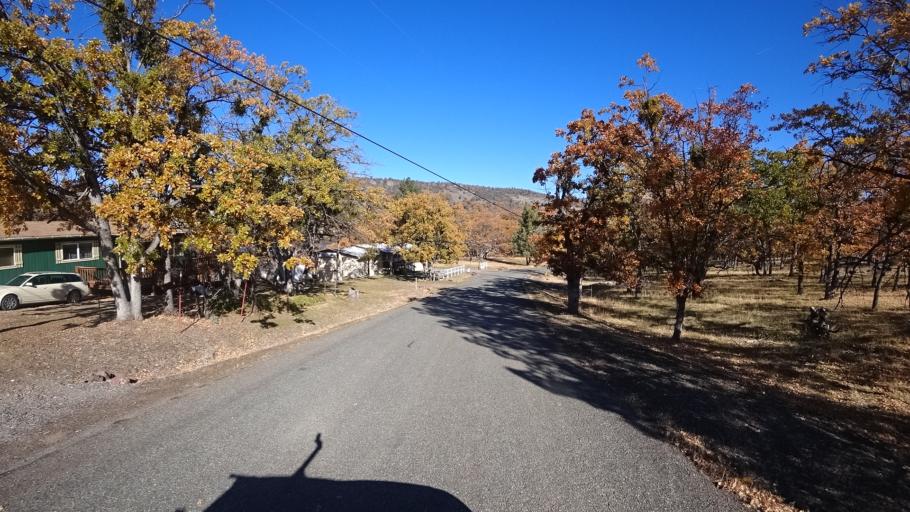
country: US
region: California
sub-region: Siskiyou County
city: Montague
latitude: 41.9781
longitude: -122.3259
